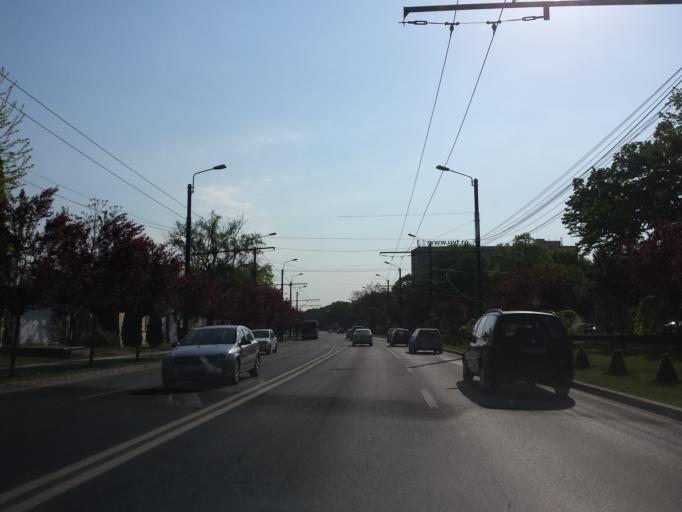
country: RO
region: Timis
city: Timisoara
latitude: 45.7477
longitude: 21.2283
